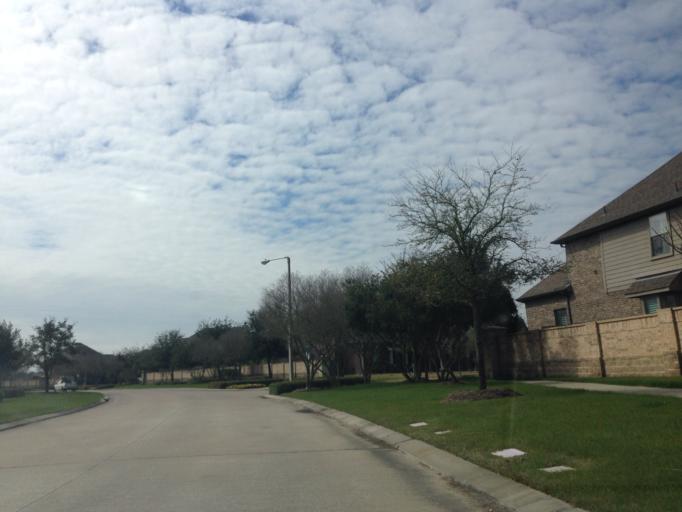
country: US
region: Texas
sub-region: Galveston County
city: Kemah
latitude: 29.5161
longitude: -95.0195
